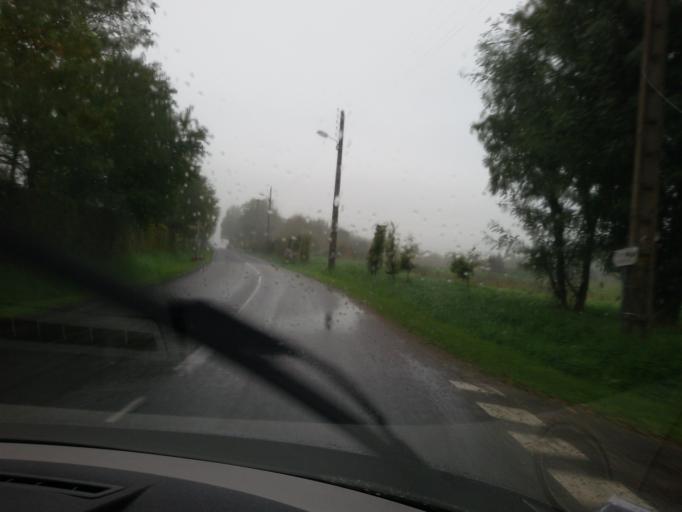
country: FR
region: Haute-Normandie
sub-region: Departement de la Seine-Maritime
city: La Cerlangue
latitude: 49.4220
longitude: 0.3911
